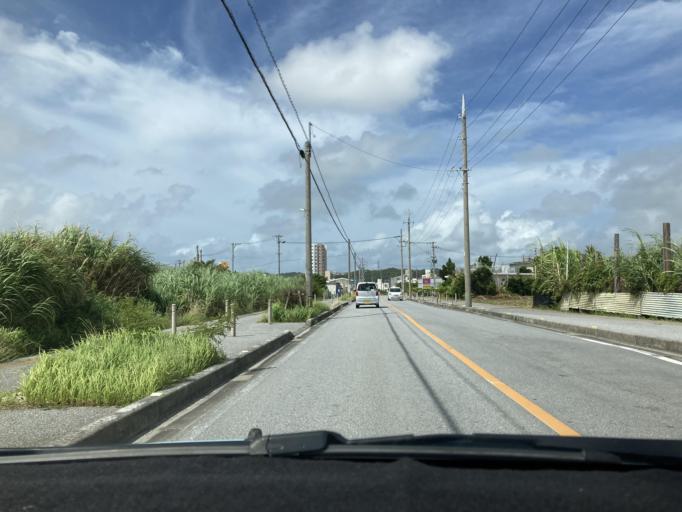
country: JP
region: Okinawa
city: Ginowan
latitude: 26.2228
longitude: 127.7711
